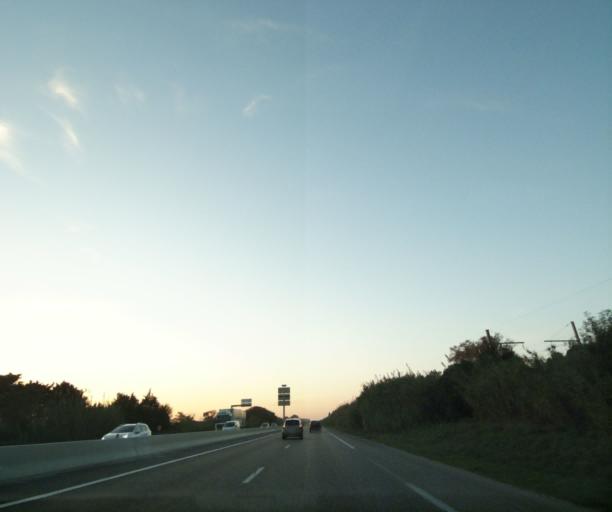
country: FR
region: Provence-Alpes-Cote d'Azur
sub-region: Departement des Bouches-du-Rhone
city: Fontvieille
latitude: 43.6425
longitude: 4.7110
